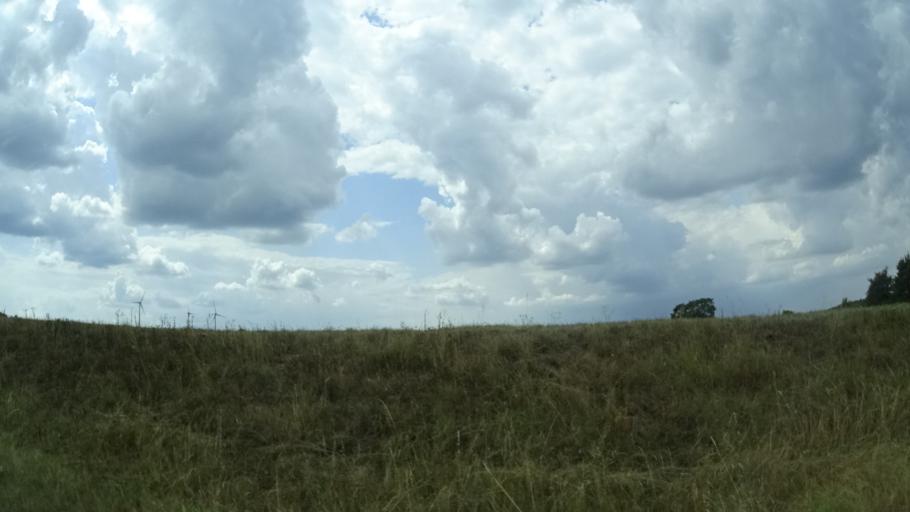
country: DE
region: Hesse
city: Gedern
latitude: 50.4132
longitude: 9.1982
